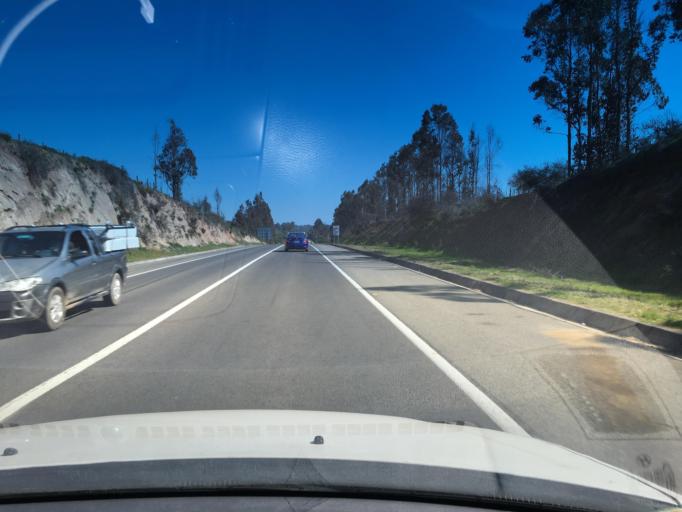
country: CL
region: Valparaiso
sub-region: San Antonio Province
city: El Tabo
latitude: -33.3930
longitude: -71.4843
